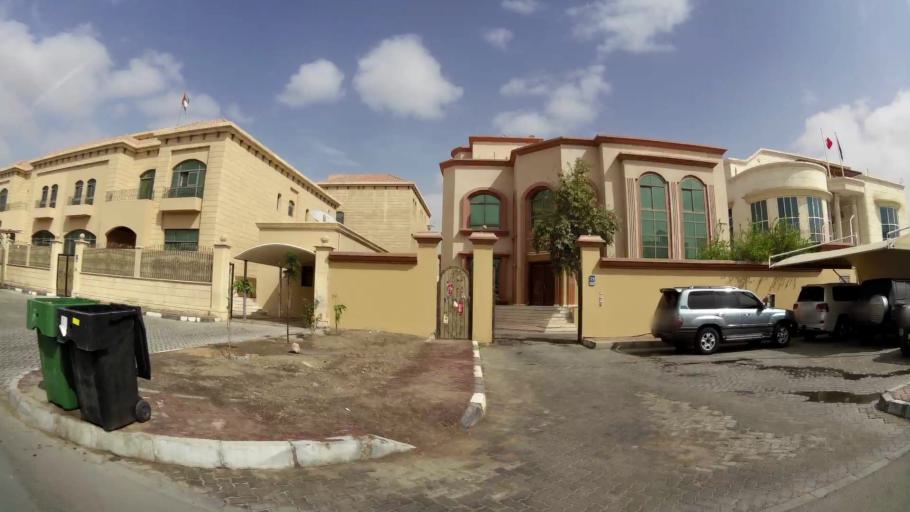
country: AE
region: Abu Dhabi
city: Abu Dhabi
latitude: 24.4060
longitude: 54.5099
